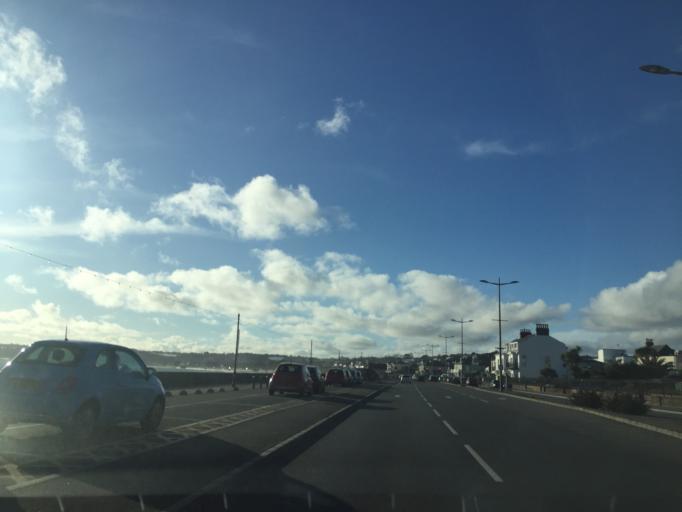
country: JE
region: St Helier
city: Saint Helier
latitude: 49.1930
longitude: -2.1268
